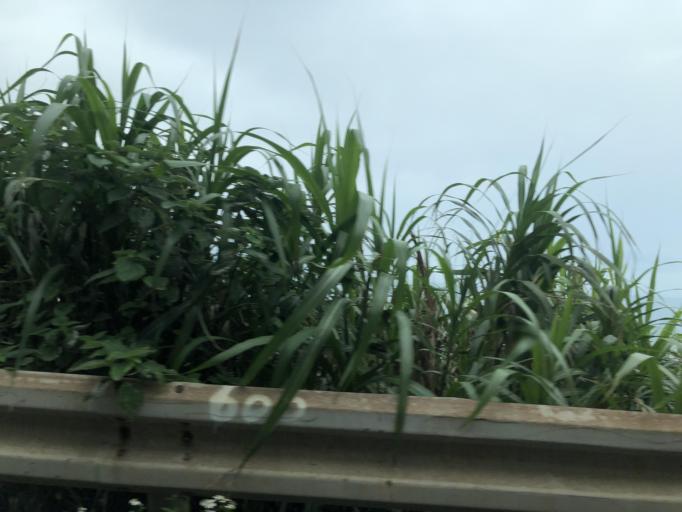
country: TW
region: Taiwan
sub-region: Keelung
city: Keelung
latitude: 25.2031
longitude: 121.6811
